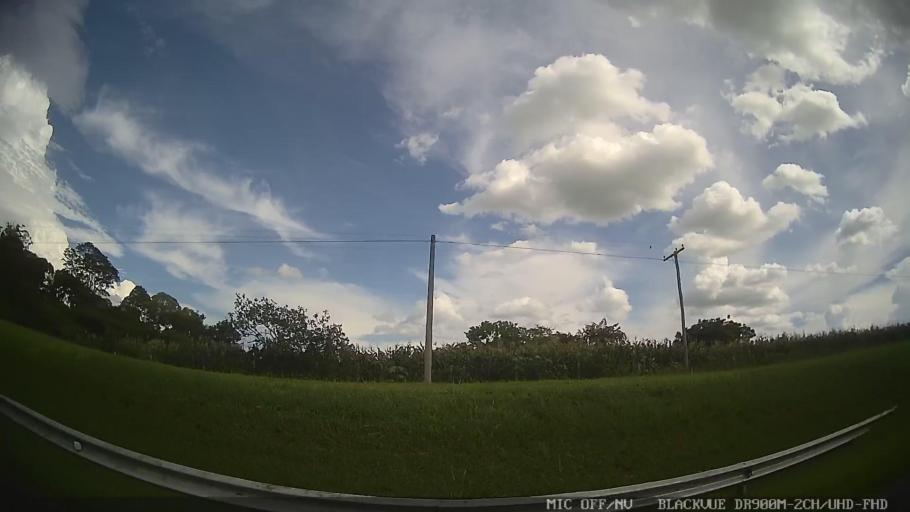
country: BR
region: Sao Paulo
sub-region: Laranjal Paulista
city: Laranjal Paulista
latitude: -23.0455
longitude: -47.9173
